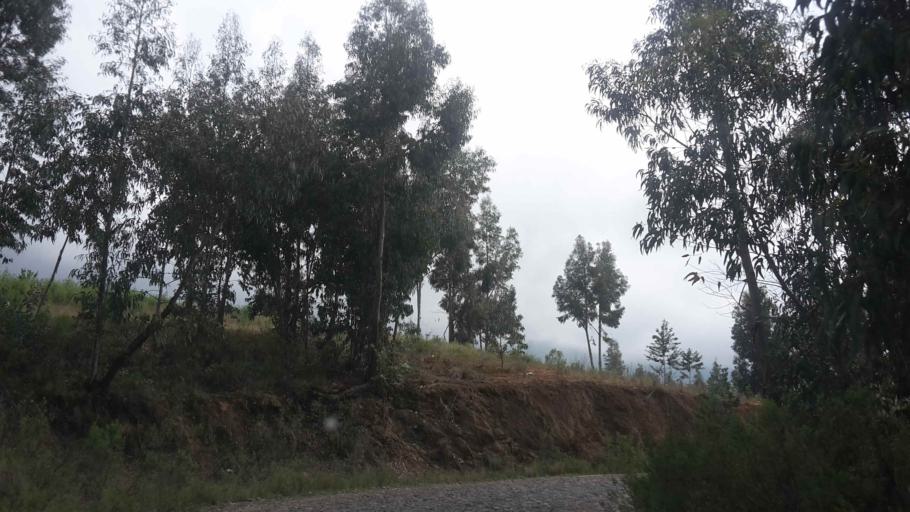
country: BO
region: Cochabamba
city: Cochabamba
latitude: -17.3573
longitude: -66.0548
